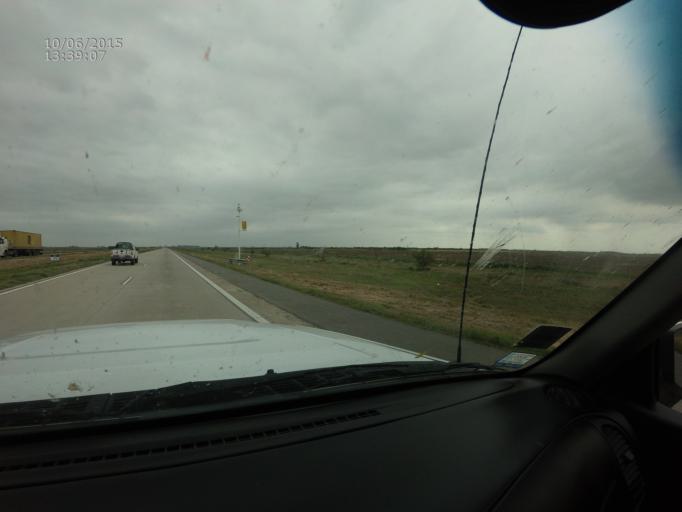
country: AR
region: Cordoba
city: Leones
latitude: -32.6014
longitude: -62.4499
